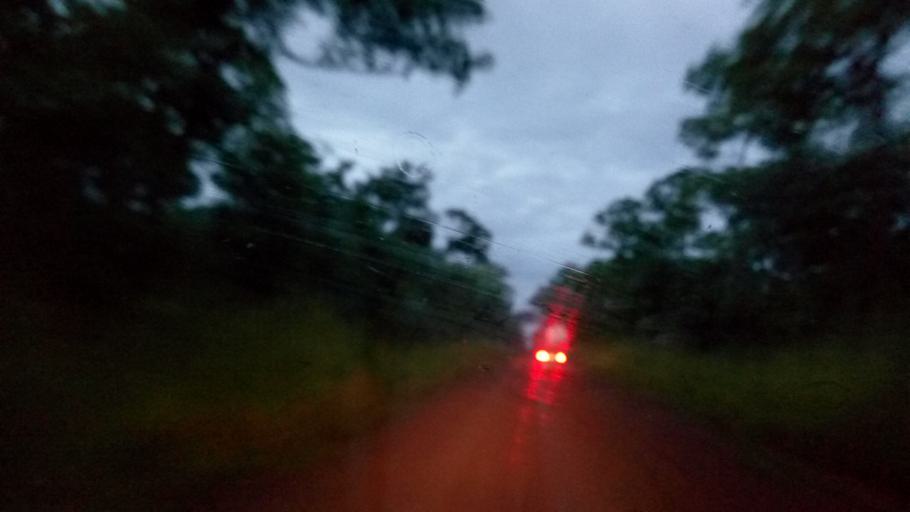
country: ZM
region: Luapula
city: Nchelenge
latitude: -9.7985
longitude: 28.1485
